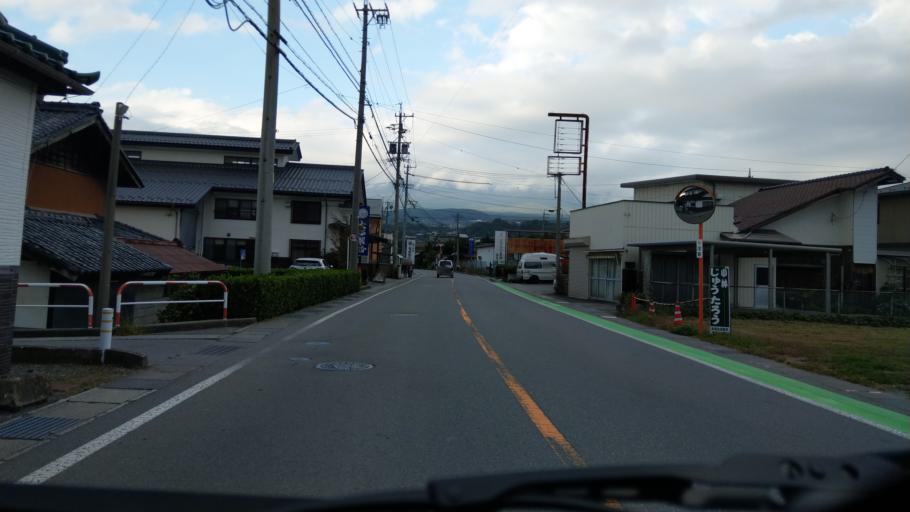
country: JP
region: Nagano
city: Komoro
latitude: 36.3137
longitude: 138.4309
